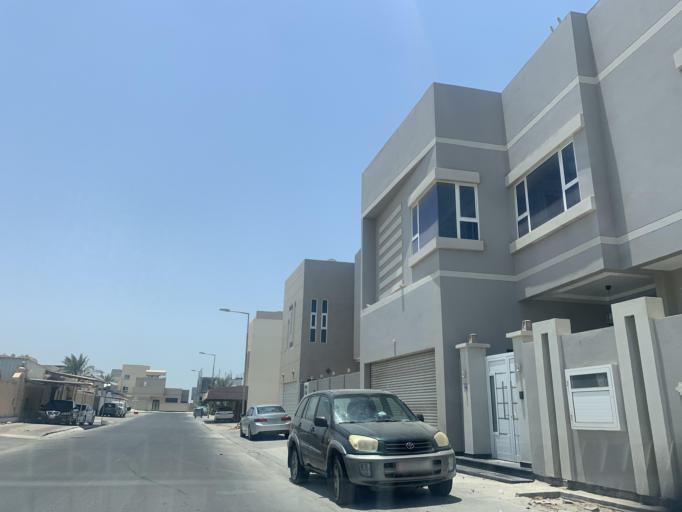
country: BH
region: Muharraq
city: Al Muharraq
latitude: 26.2871
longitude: 50.6201
